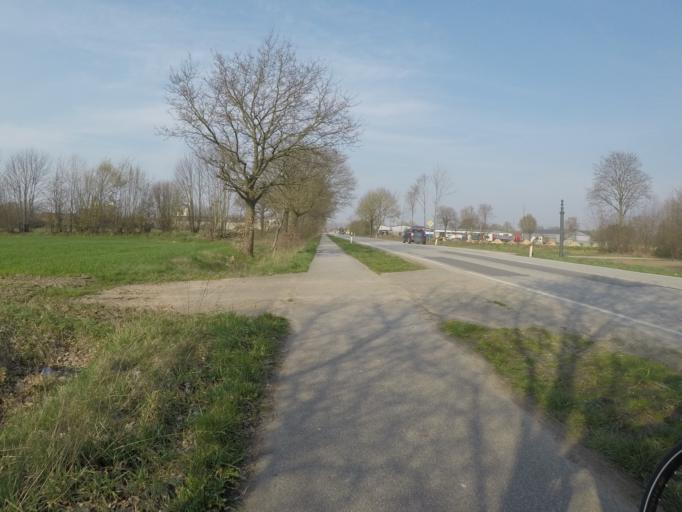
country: DE
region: Schleswig-Holstein
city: Leezen
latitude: 53.8608
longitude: 10.2484
